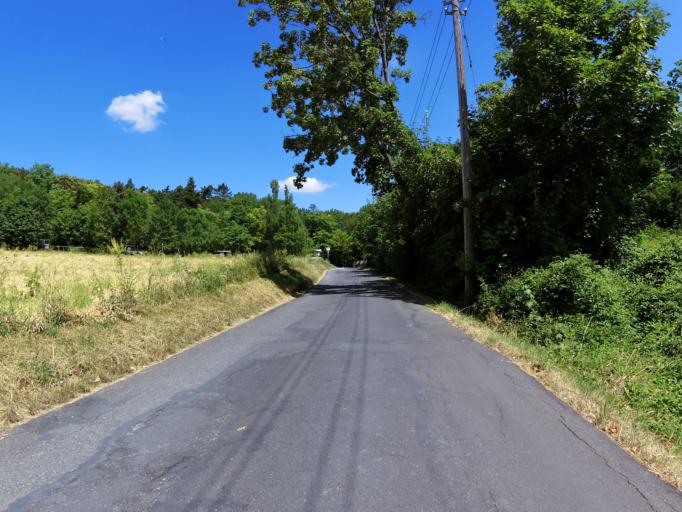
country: DE
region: Bavaria
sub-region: Regierungsbezirk Unterfranken
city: Wuerzburg
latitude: 49.7812
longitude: 9.9217
